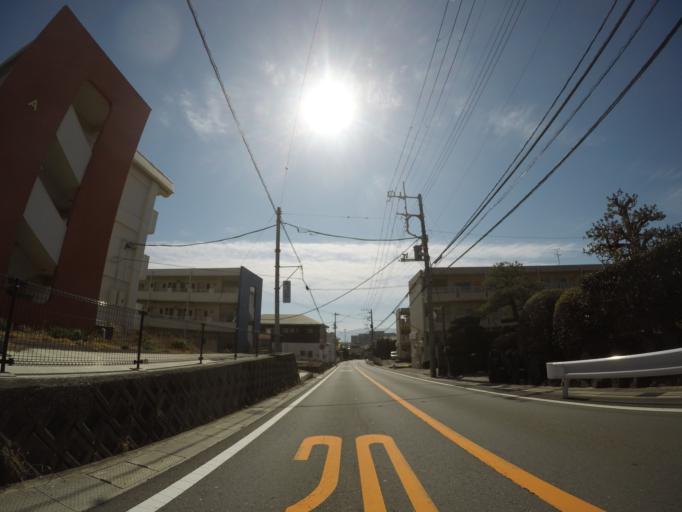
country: JP
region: Shizuoka
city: Numazu
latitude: 35.1257
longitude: 138.8353
